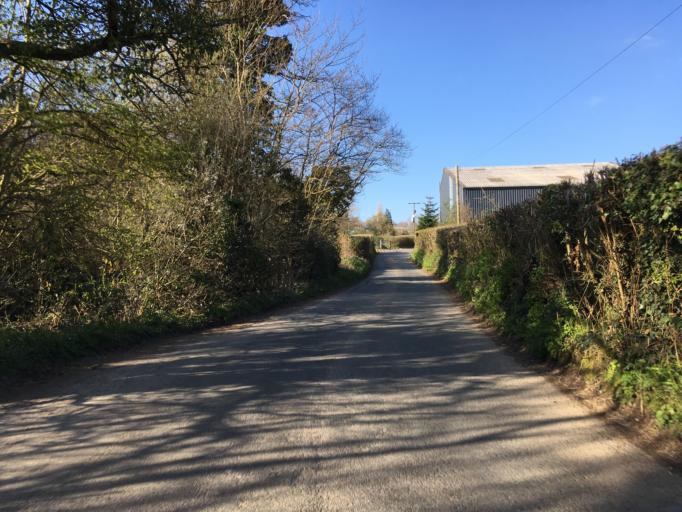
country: GB
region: Wales
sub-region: Torfaen County Borough
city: New Inn
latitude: 51.7007
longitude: -2.9845
